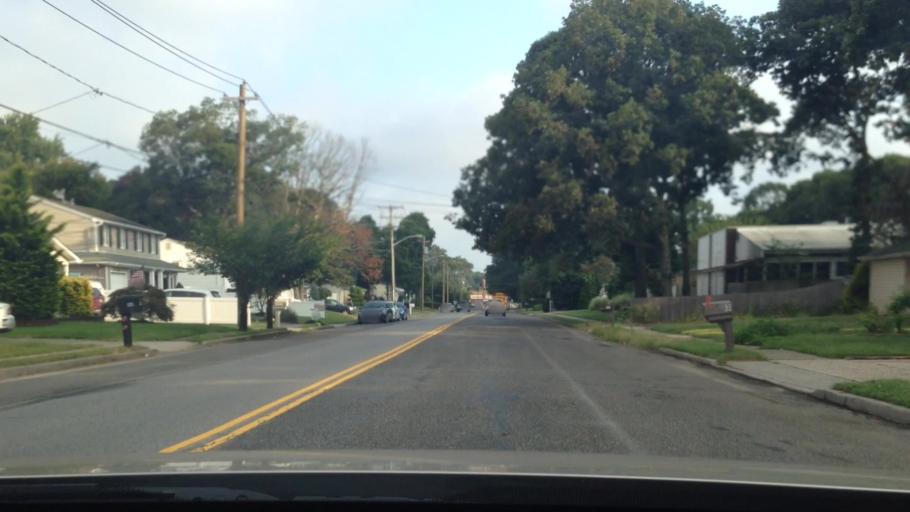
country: US
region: New York
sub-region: Suffolk County
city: Selden
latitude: 40.8599
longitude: -73.0470
